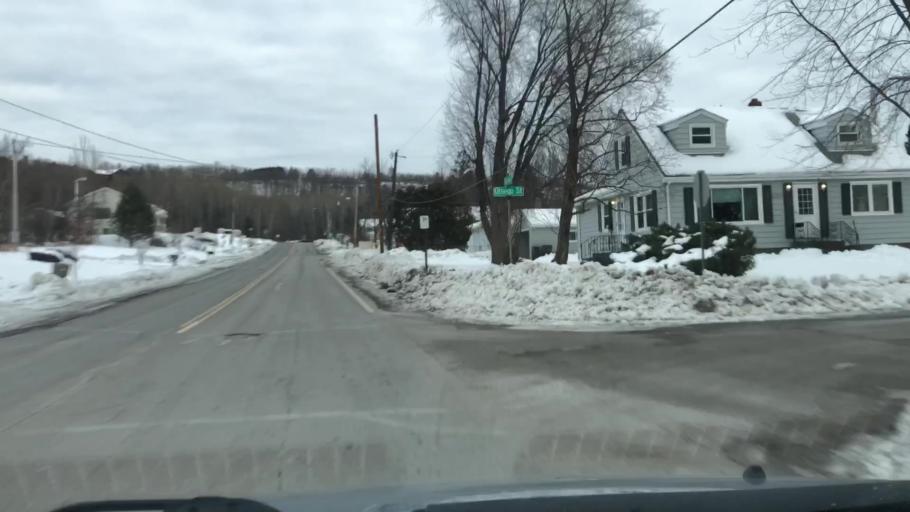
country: US
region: Minnesota
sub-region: Saint Louis County
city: Arnold
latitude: 46.8383
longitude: -92.0369
